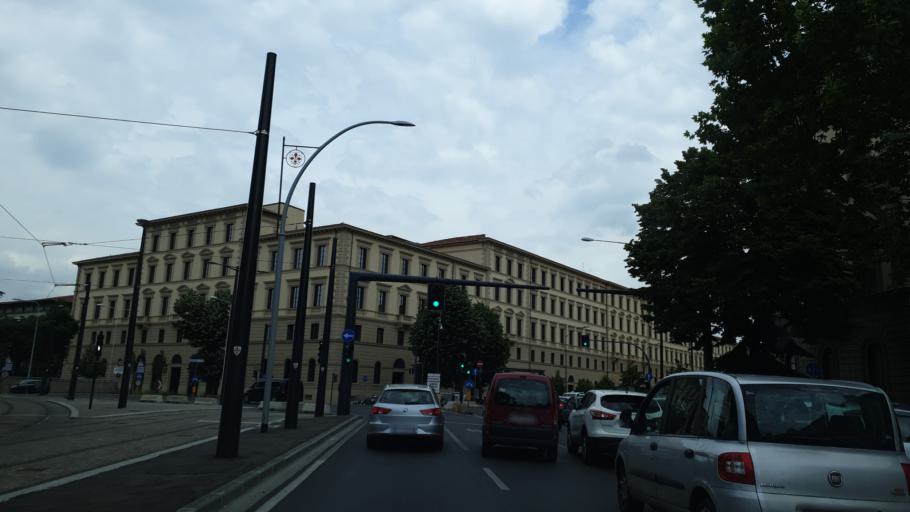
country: IT
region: Tuscany
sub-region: Province of Florence
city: Florence
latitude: 43.7814
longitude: 11.2525
